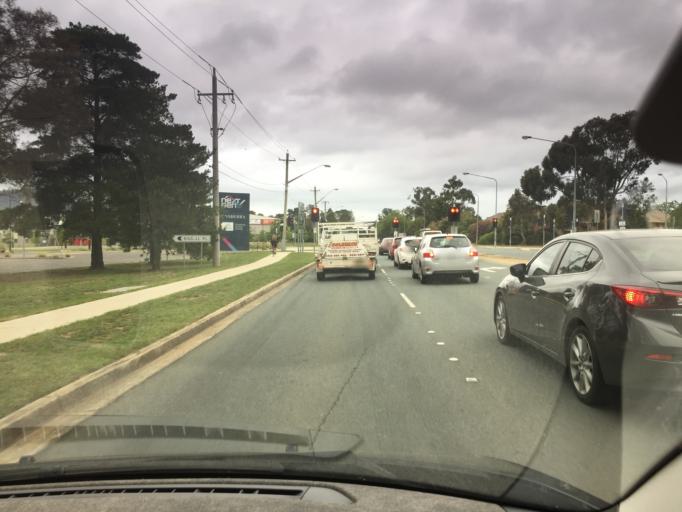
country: AU
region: Australian Capital Territory
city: Kaleen
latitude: -35.2421
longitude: 149.1265
